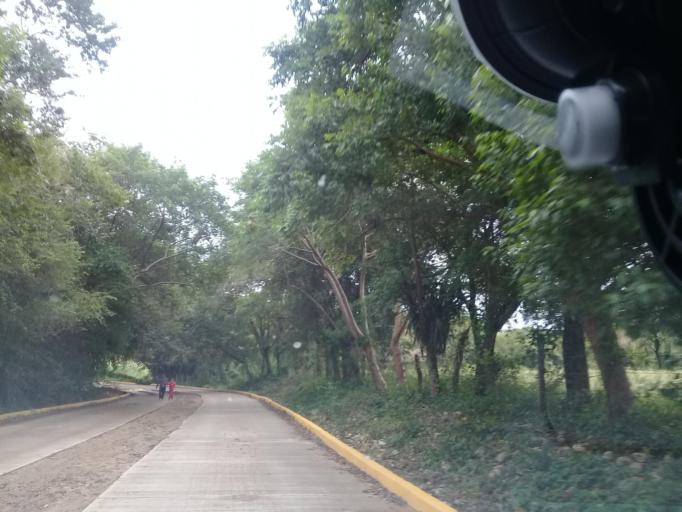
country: MX
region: Hidalgo
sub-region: Huejutla de Reyes
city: Chalahuiyapa
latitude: 21.1624
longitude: -98.3551
